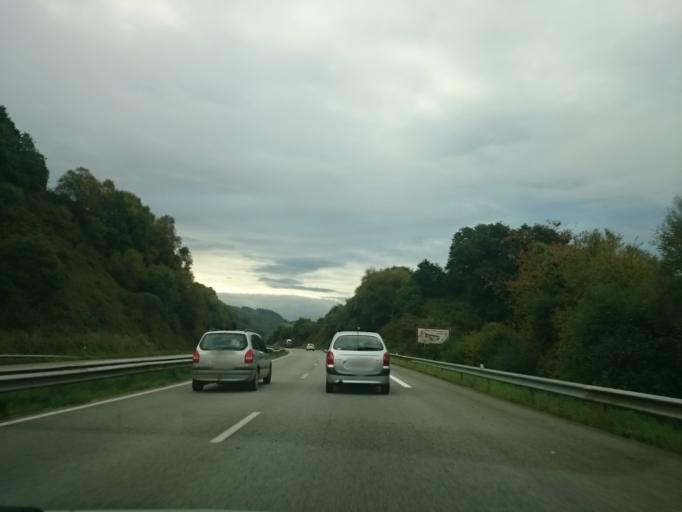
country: FR
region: Brittany
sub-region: Departement du Finistere
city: Dineault
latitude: 48.2522
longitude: -4.1143
